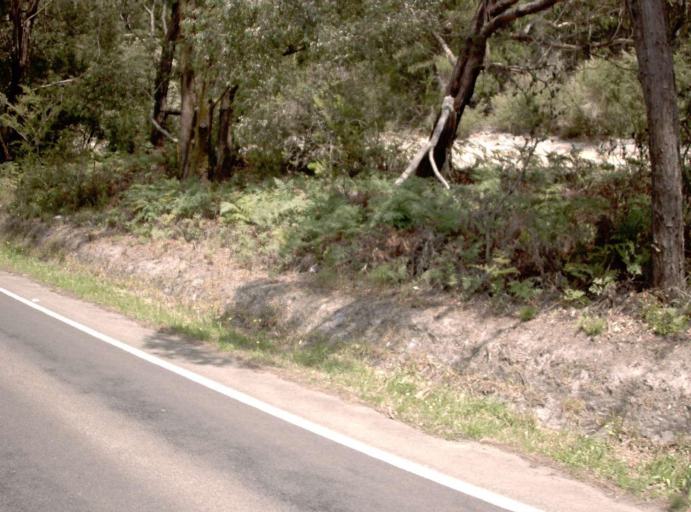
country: AU
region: Victoria
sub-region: Latrobe
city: Traralgon
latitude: -38.2730
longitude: 146.6923
